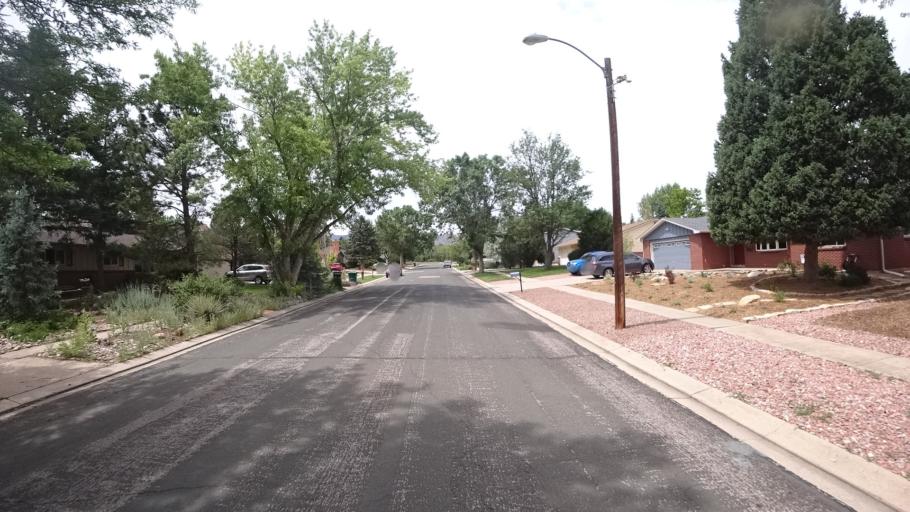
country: US
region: Colorado
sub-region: El Paso County
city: Manitou Springs
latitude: 38.8699
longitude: -104.8700
